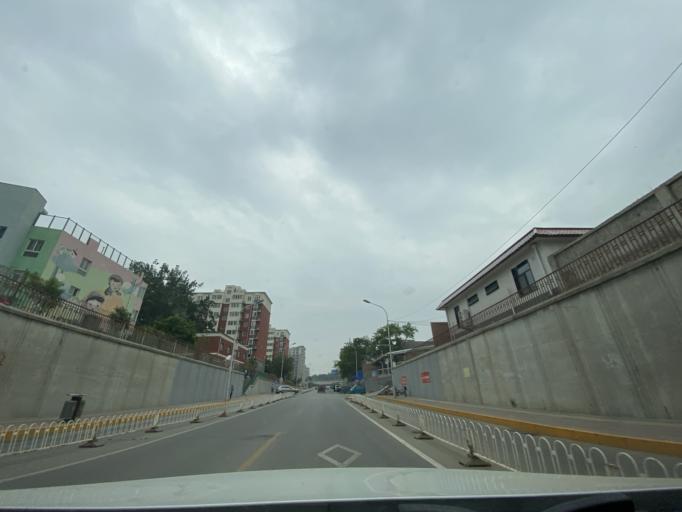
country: CN
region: Beijing
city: Sijiqing
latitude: 39.9307
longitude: 116.2421
